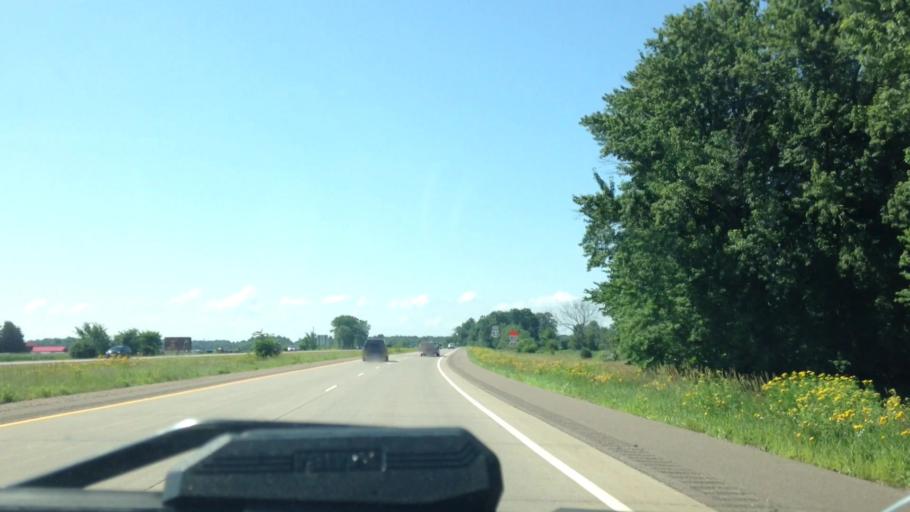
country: US
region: Wisconsin
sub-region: Barron County
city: Rice Lake
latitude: 45.4635
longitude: -91.7581
